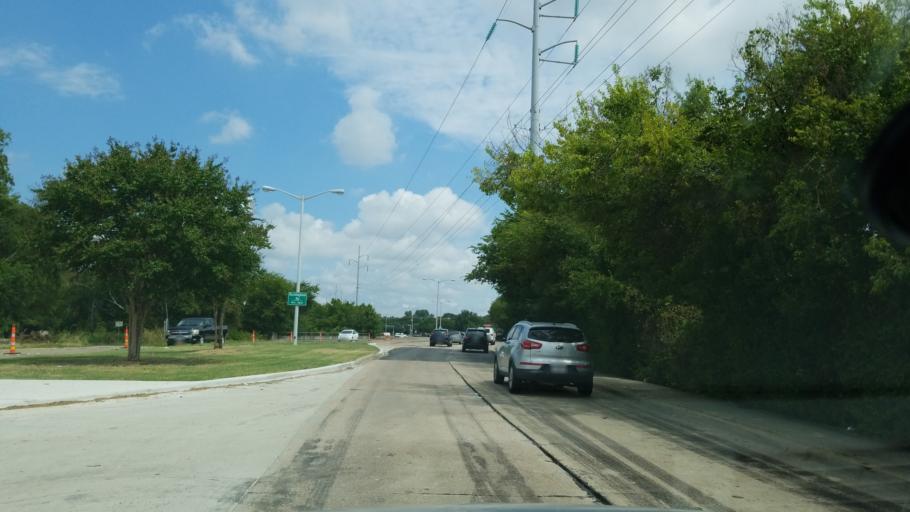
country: US
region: Texas
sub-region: Dallas County
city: Garland
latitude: 32.9274
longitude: -96.6652
